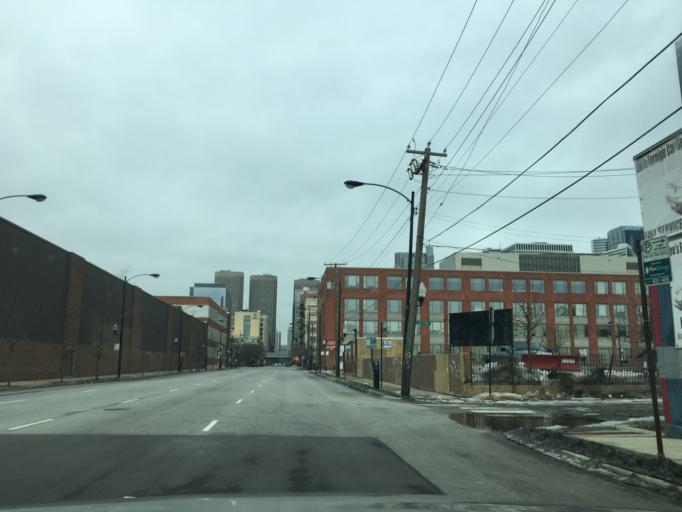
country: US
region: Illinois
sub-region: Cook County
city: Chicago
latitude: 41.8727
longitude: -87.6423
